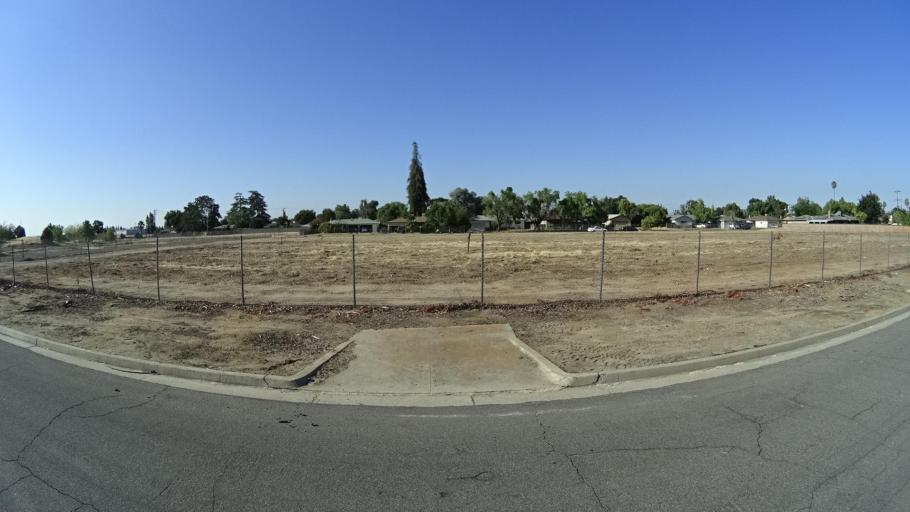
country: US
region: California
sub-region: Fresno County
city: Tarpey Village
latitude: 36.7851
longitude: -119.7380
